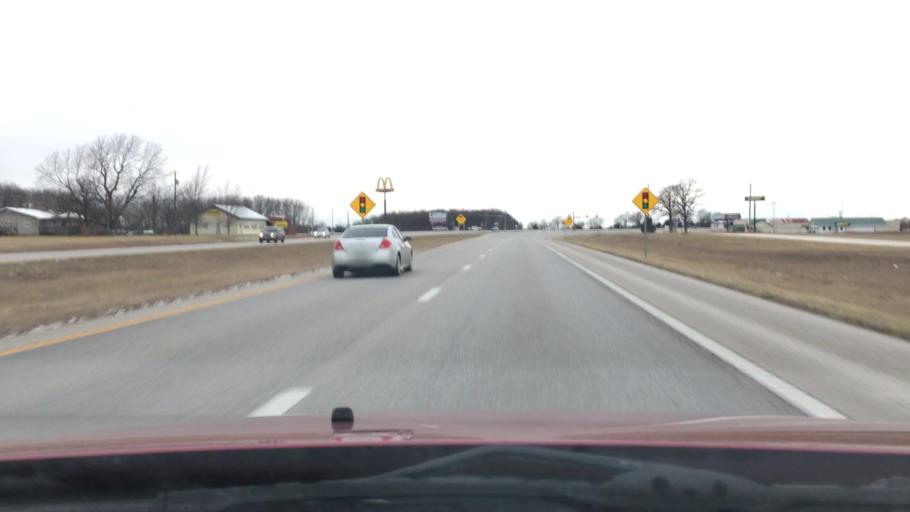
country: US
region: Missouri
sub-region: Webster County
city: Seymour
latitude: 37.1566
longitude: -92.7826
